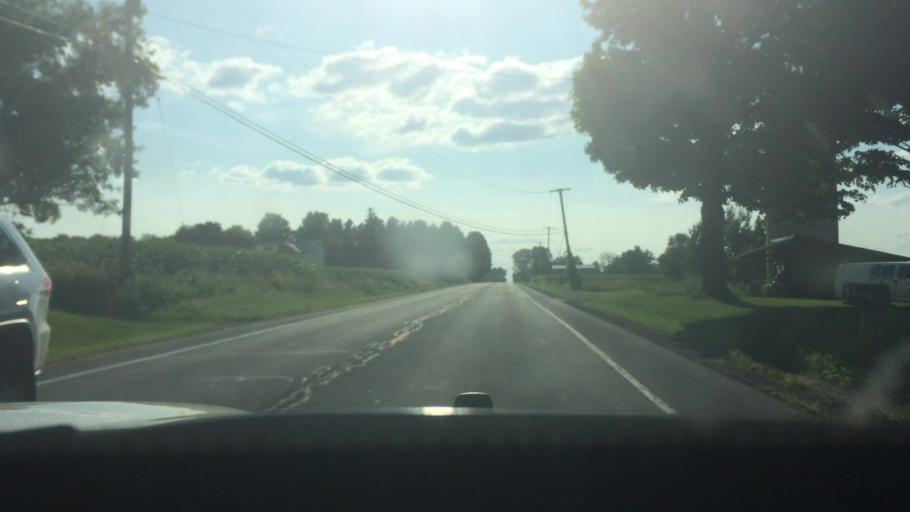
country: US
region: New York
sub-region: St. Lawrence County
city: Hannawa Falls
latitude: 44.6916
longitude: -74.6859
